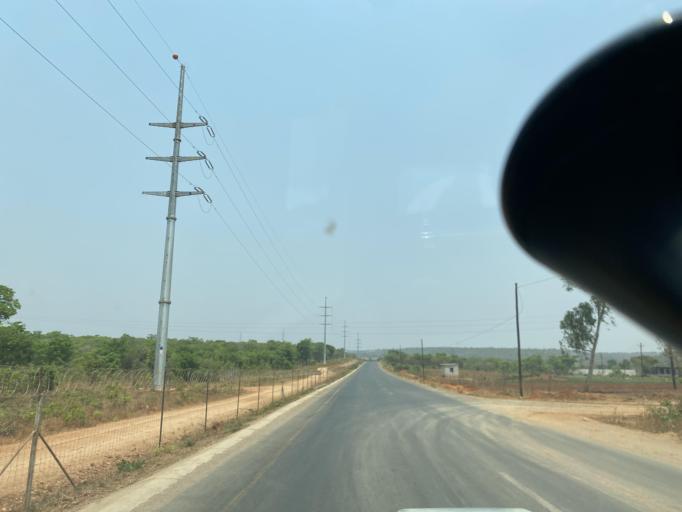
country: ZM
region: Lusaka
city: Lusaka
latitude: -15.5372
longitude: 28.4713
